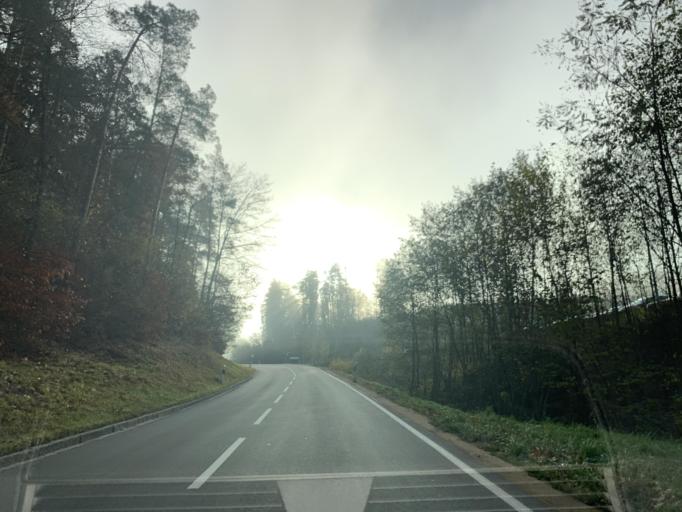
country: DE
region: Bavaria
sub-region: Upper Palatinate
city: Neunburg vorm Wald
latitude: 49.3425
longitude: 12.3993
